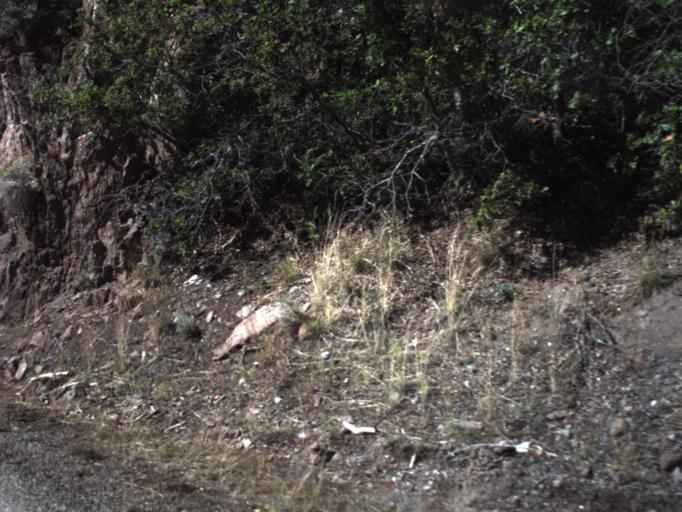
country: US
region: Utah
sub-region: Beaver County
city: Beaver
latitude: 38.2519
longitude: -112.5374
